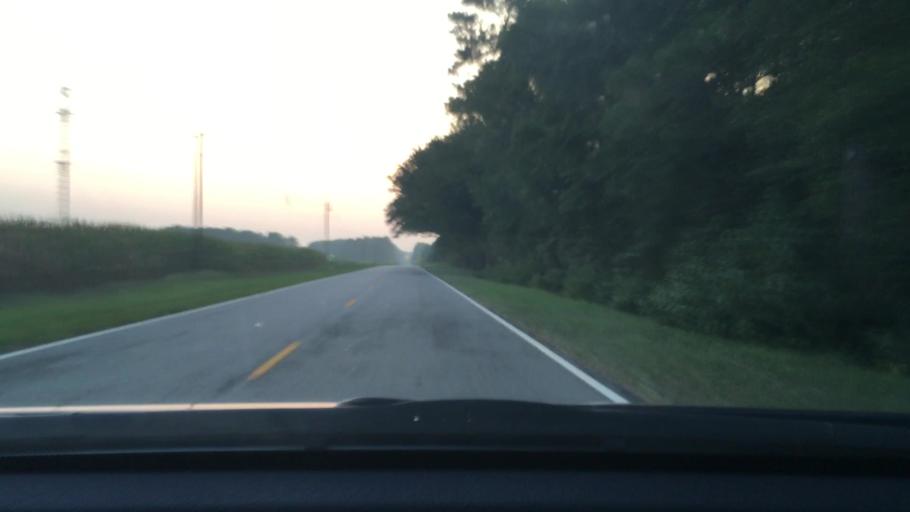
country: US
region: South Carolina
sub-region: Lee County
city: Bishopville
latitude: 34.1152
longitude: -80.1496
